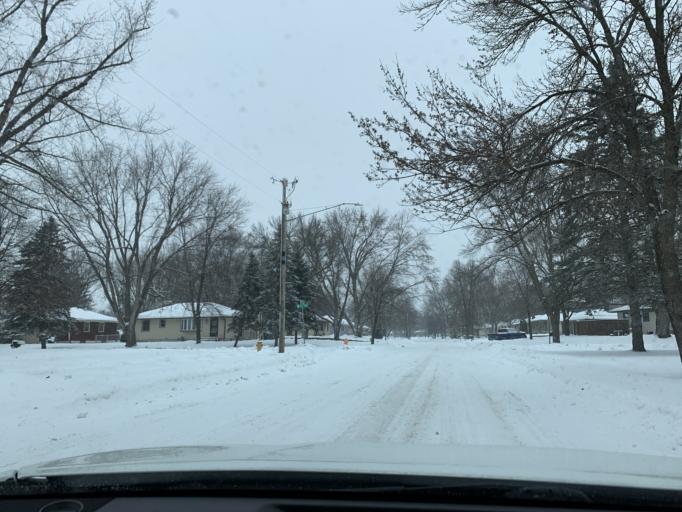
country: US
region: Minnesota
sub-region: Anoka County
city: Coon Rapids
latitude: 45.1717
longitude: -93.2878
